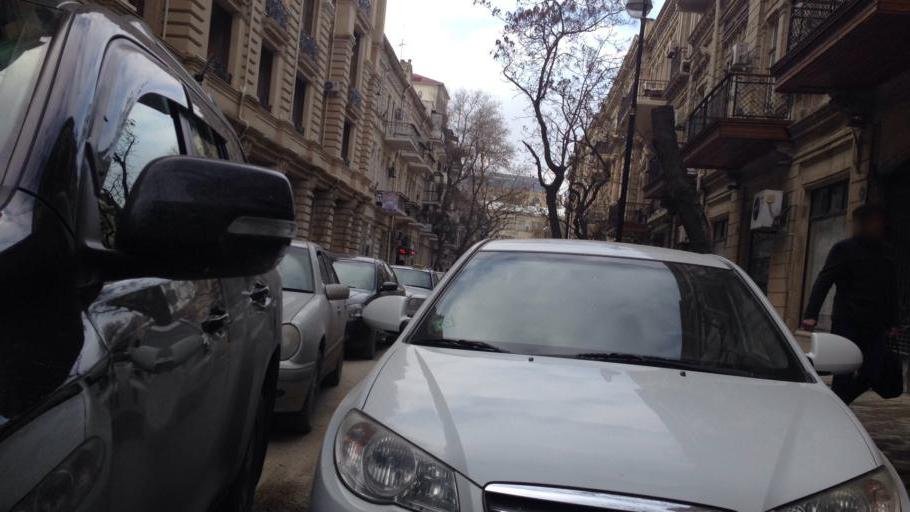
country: AZ
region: Baki
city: Badamdar
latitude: 40.3716
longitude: 49.8425
